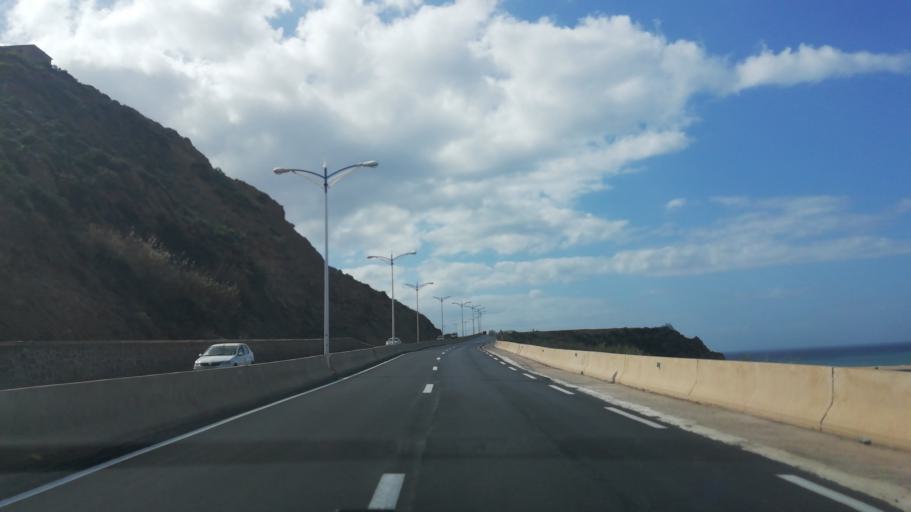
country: DZ
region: Mostaganem
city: Mostaganem
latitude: 36.0109
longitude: 0.1284
